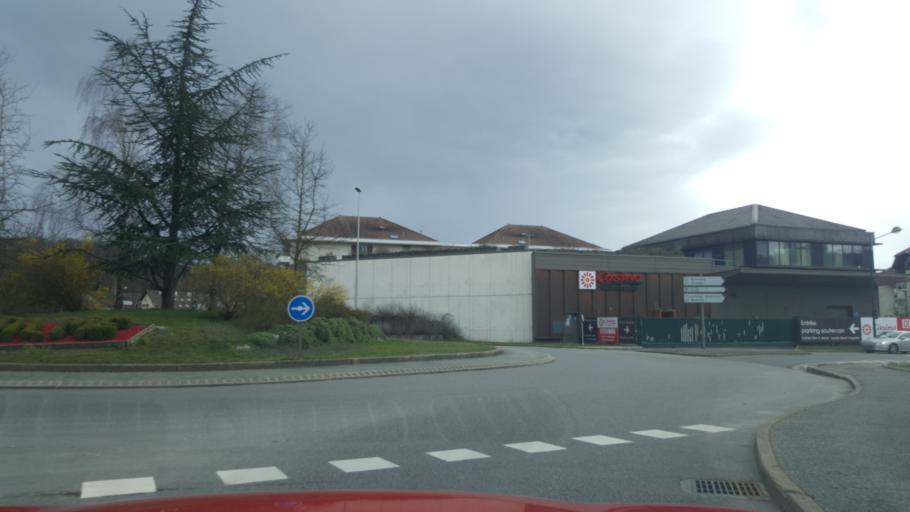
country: FR
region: Rhone-Alpes
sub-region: Departement de la Haute-Savoie
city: La Balme-de-Sillingy
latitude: 45.9624
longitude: 6.0392
